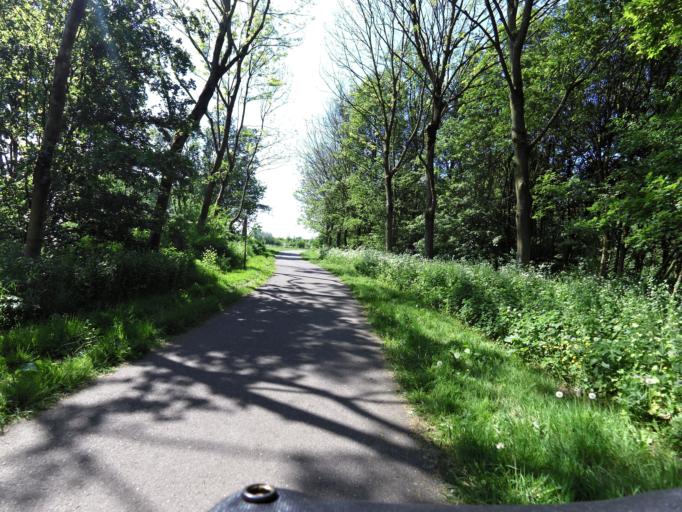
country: NL
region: South Holland
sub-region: Gemeente Barendrecht
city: Barendrecht
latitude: 51.8339
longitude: 4.5216
